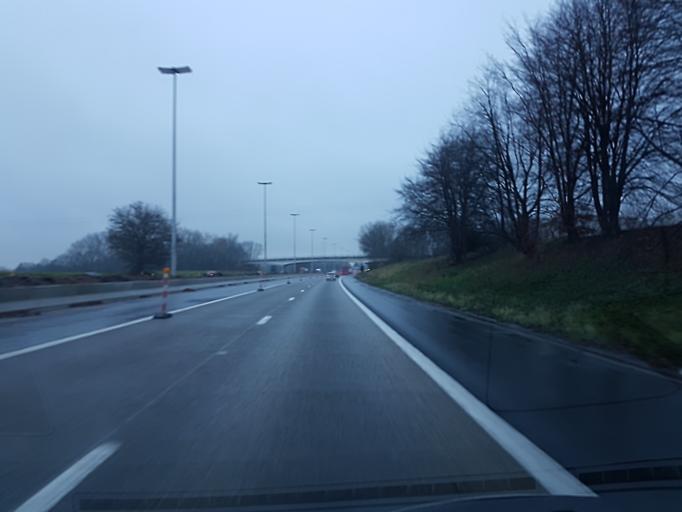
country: BE
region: Wallonia
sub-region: Province de Namur
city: Eghezee
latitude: 50.5229
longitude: 4.9133
